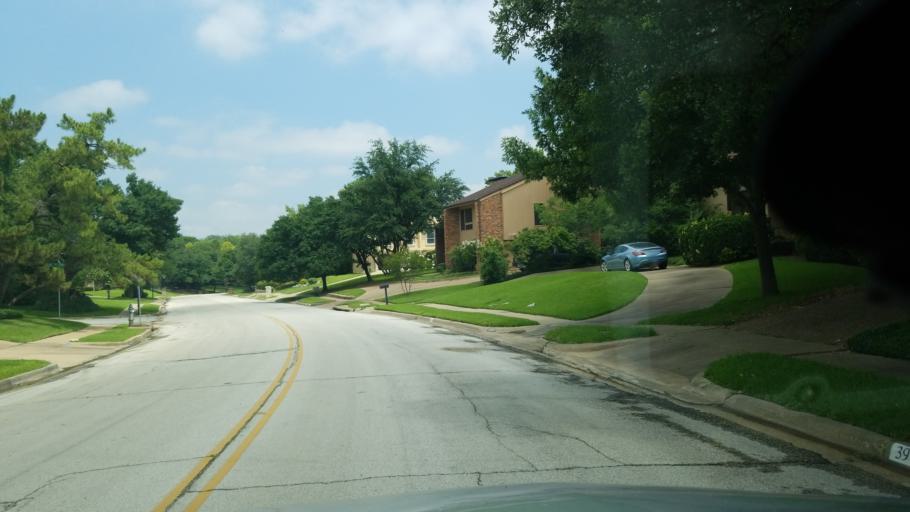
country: US
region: Texas
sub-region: Dallas County
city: Irving
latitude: 32.8544
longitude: -96.9416
